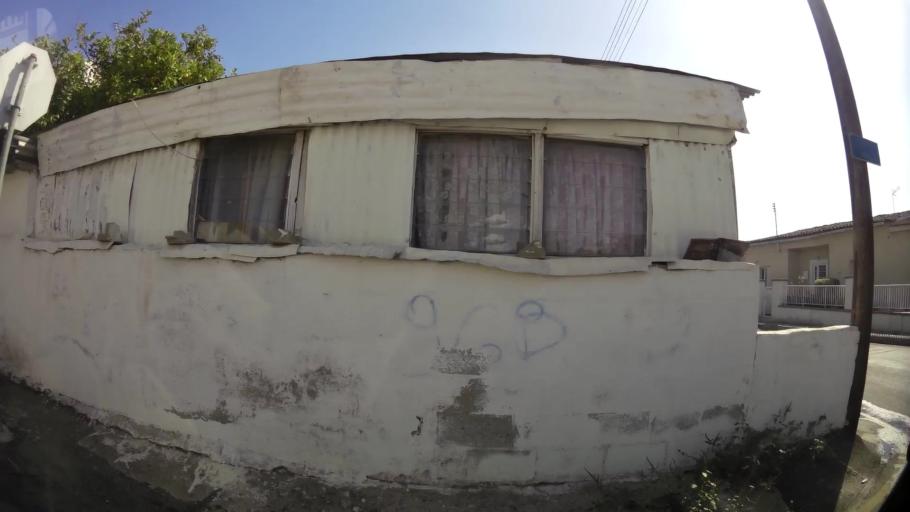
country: CY
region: Larnaka
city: Aradippou
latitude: 34.9524
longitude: 33.5860
